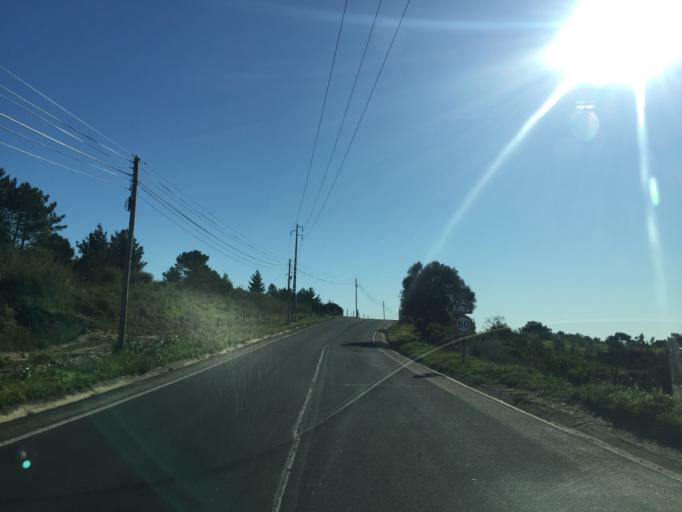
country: PT
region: Lisbon
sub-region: Sintra
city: Belas
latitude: 38.8047
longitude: -9.2870
